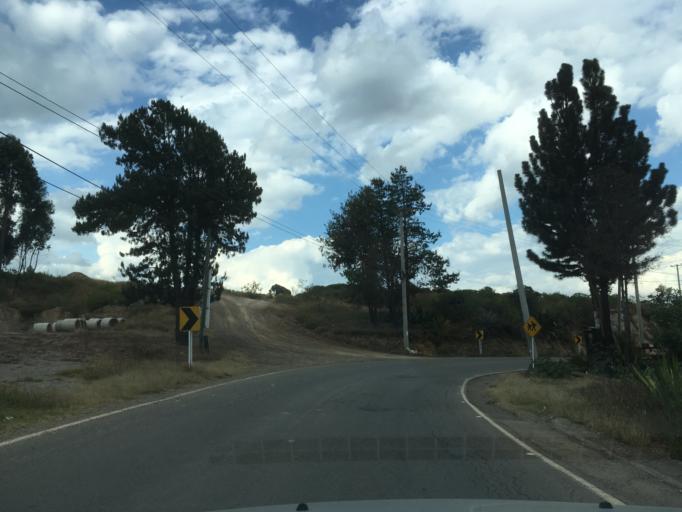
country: CO
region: Boyaca
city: Raquira
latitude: 5.5748
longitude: -73.6485
